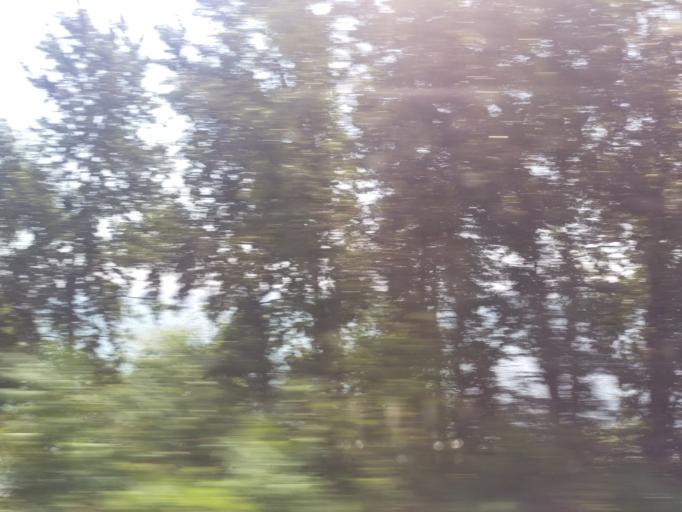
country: CA
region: Ontario
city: Scarborough
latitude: 43.7686
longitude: -79.1429
